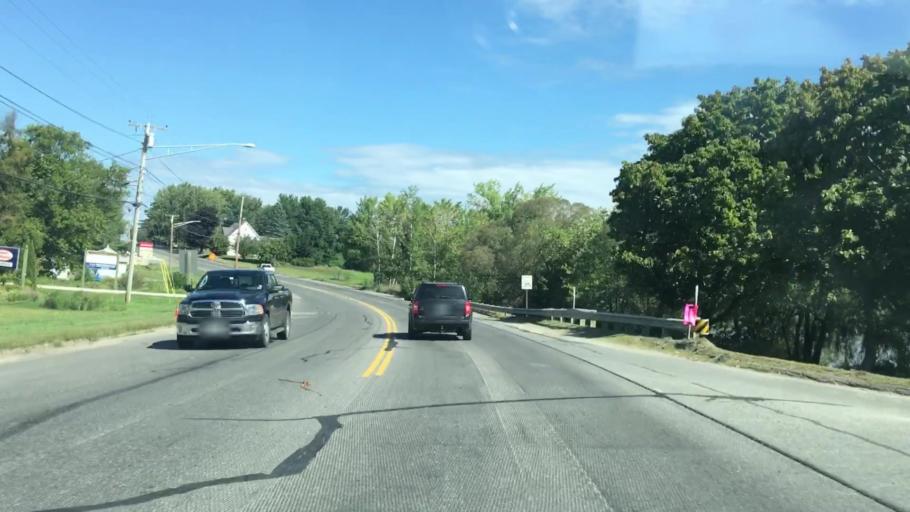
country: US
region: Maine
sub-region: Penobscot County
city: Newport
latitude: 44.8410
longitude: -69.2808
